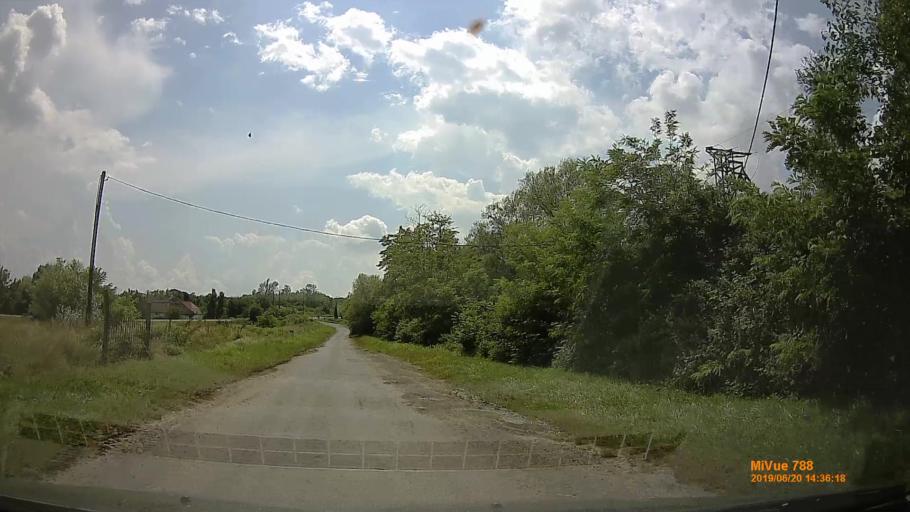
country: HU
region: Baranya
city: Hosszuheteny
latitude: 46.1101
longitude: 18.3198
